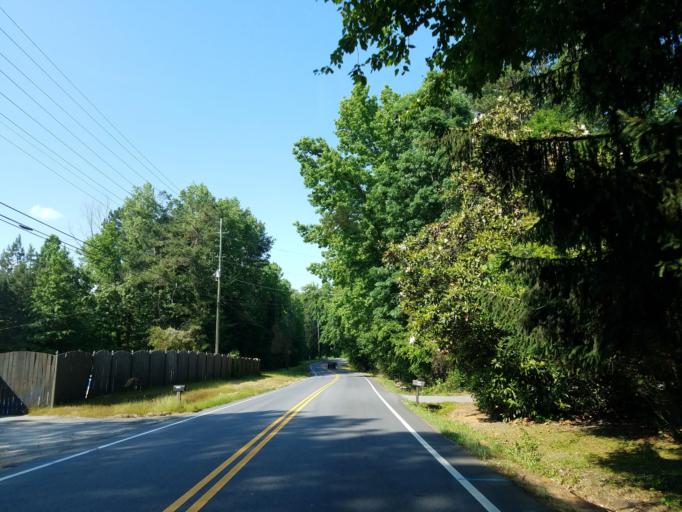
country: US
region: Georgia
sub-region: Cherokee County
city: Holly Springs
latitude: 34.1892
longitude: -84.5423
